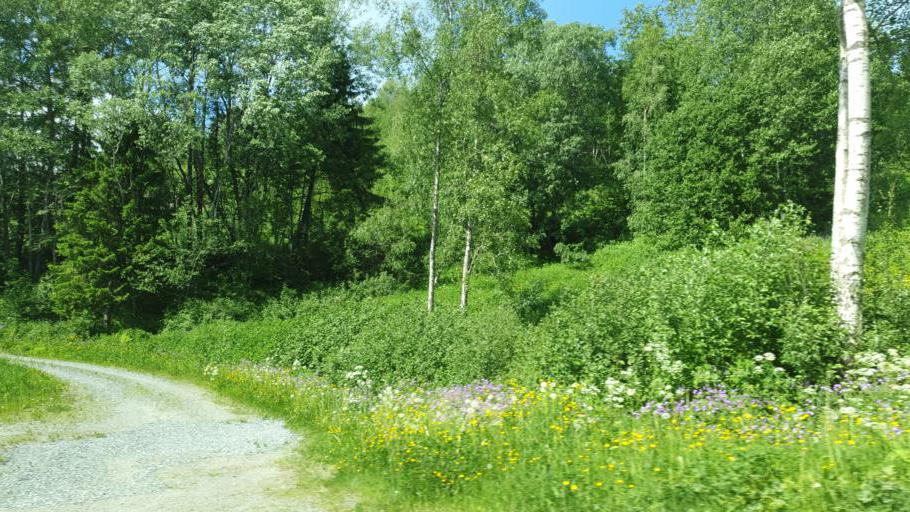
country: NO
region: Nord-Trondelag
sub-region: Leksvik
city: Leksvik
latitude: 63.6911
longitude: 10.6775
